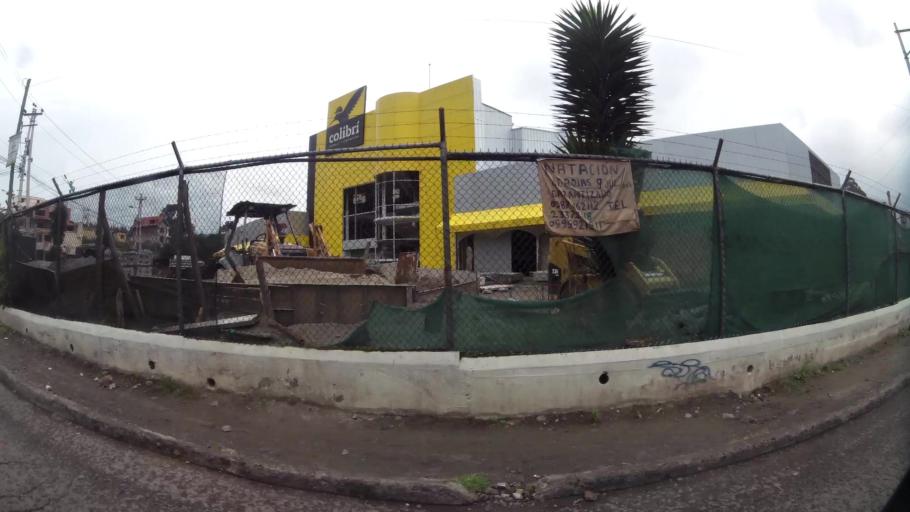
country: EC
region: Pichincha
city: Sangolqui
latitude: -0.3327
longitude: -78.4348
